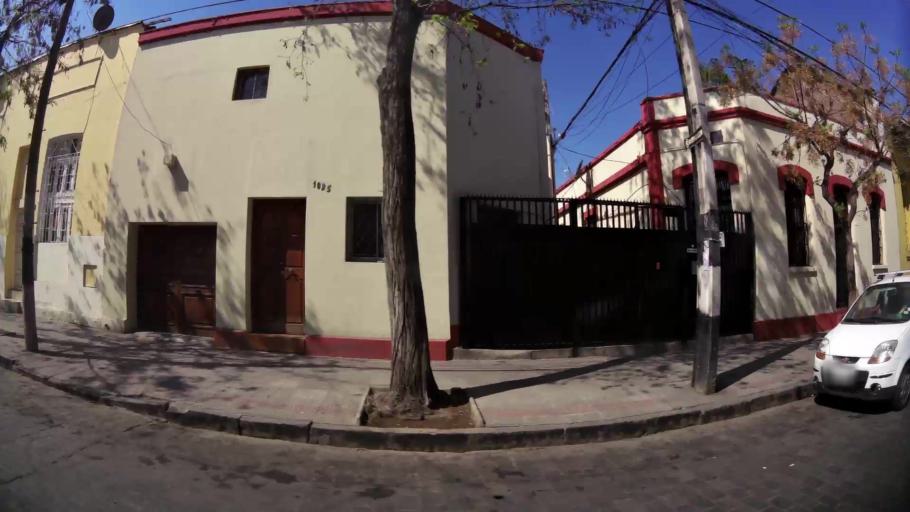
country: CL
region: Santiago Metropolitan
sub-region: Provincia de Santiago
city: Santiago
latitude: -33.4323
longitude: -70.6630
